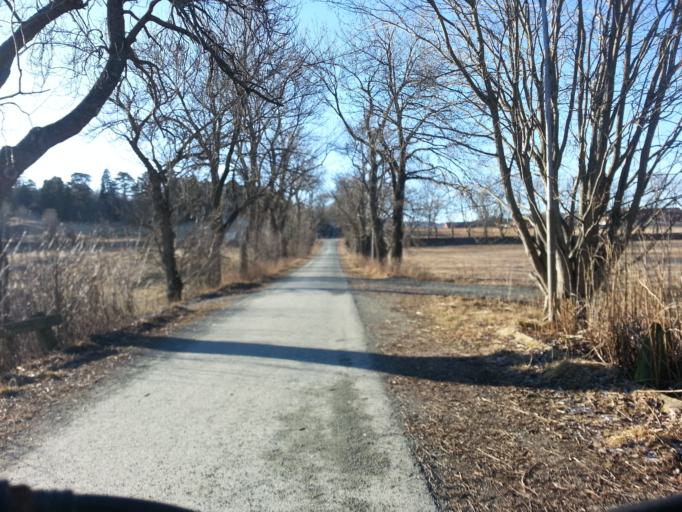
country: NO
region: Sor-Trondelag
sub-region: Trondheim
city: Trondheim
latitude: 63.4365
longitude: 10.4836
